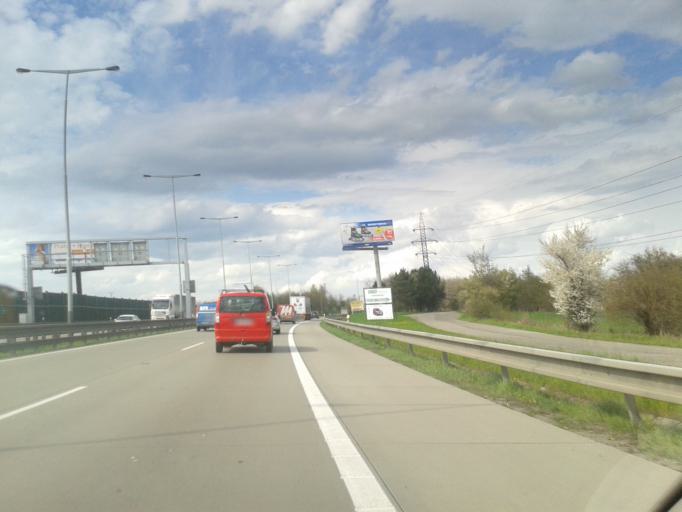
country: CZ
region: Central Bohemia
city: Rudna
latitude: 50.0379
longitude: 14.2720
